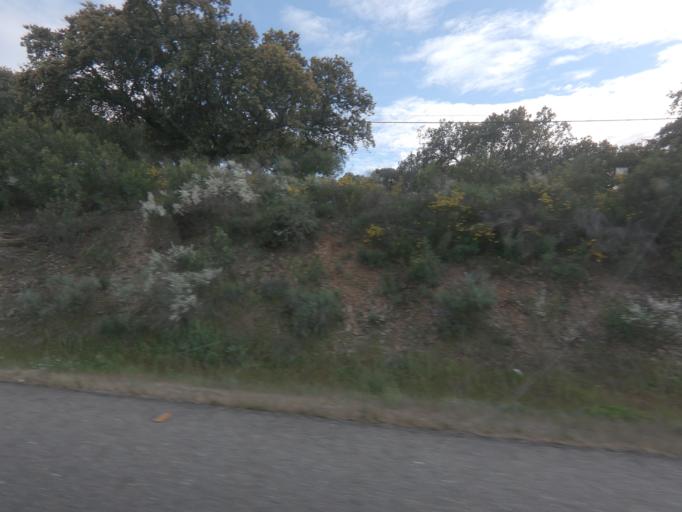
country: ES
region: Extremadura
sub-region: Provincia de Caceres
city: Pedroso de Acim
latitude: 39.8318
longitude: -6.3841
